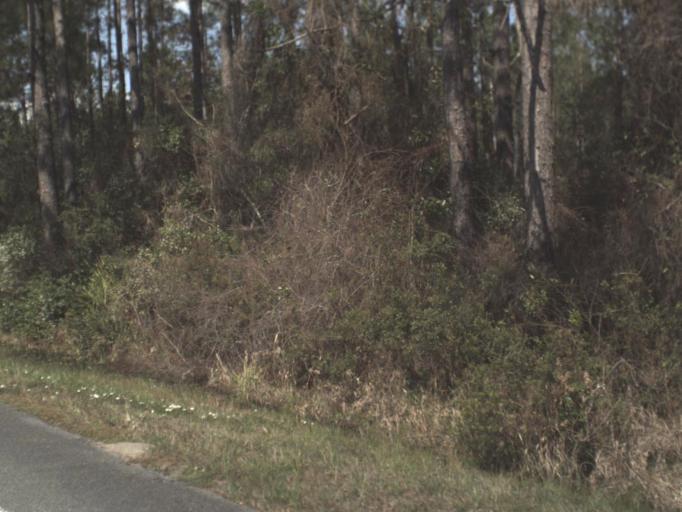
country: US
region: Florida
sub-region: Franklin County
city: Carrabelle
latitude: 29.9762
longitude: -84.4995
